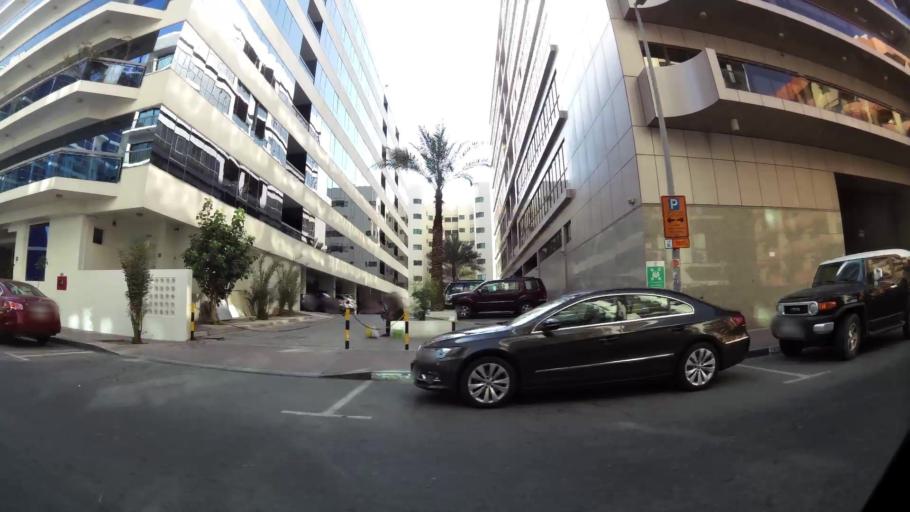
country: AE
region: Ash Shariqah
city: Sharjah
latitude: 25.2515
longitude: 55.2950
